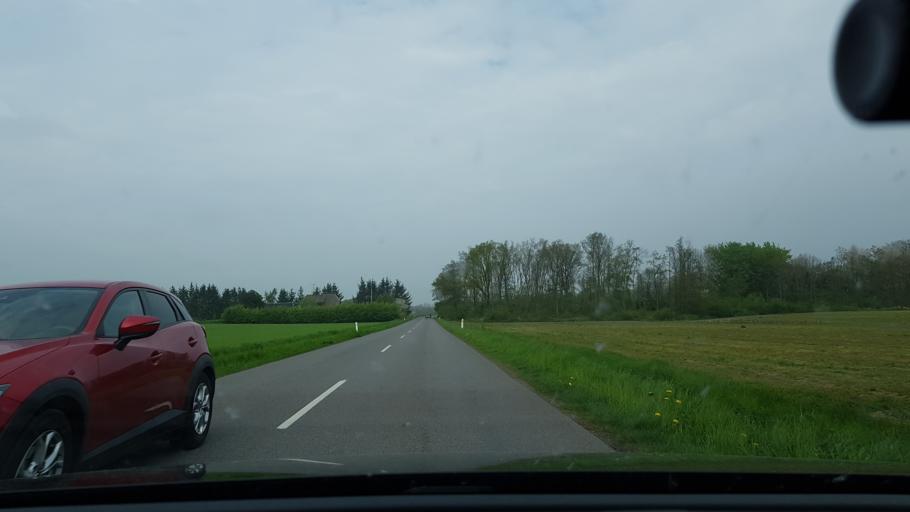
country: DK
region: Capital Region
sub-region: Bornholm Kommune
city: Nexo
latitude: 55.0173
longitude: 15.0964
